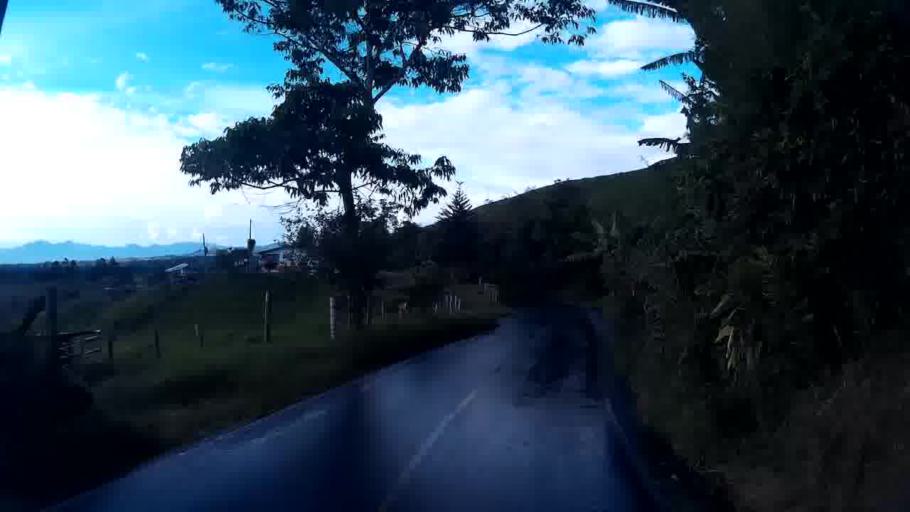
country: CO
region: Quindio
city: Filandia
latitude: 4.6799
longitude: -75.6586
